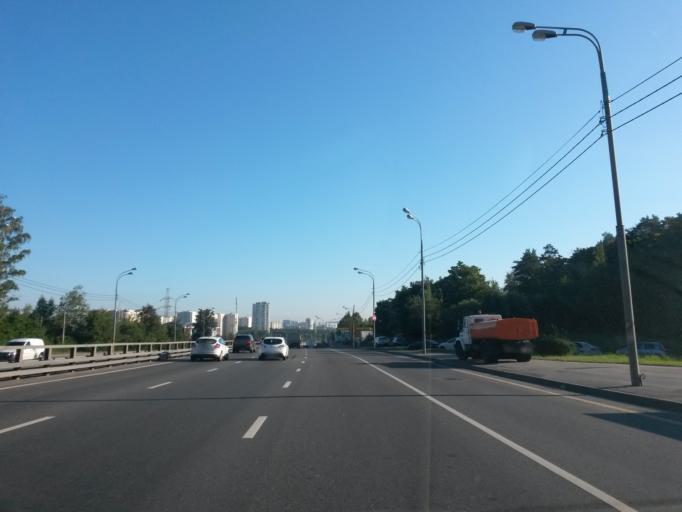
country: RU
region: Moscow
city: Annino
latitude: 55.5502
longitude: 37.5869
